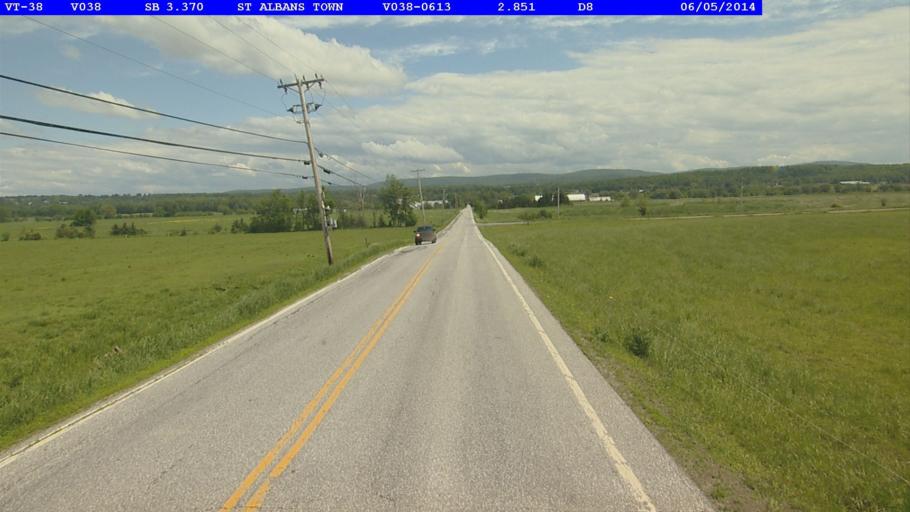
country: US
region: Vermont
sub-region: Franklin County
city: Saint Albans
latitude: 44.8522
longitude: -73.1284
